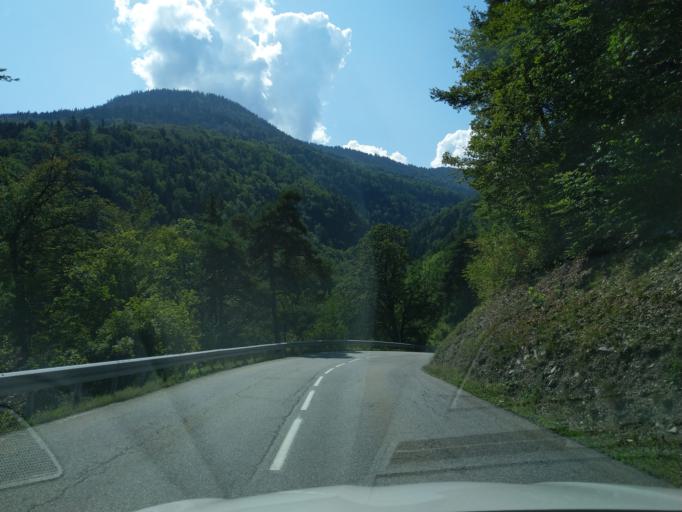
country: FR
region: Rhone-Alpes
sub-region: Departement de la Savoie
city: Les Allues
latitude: 45.4472
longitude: 6.5627
